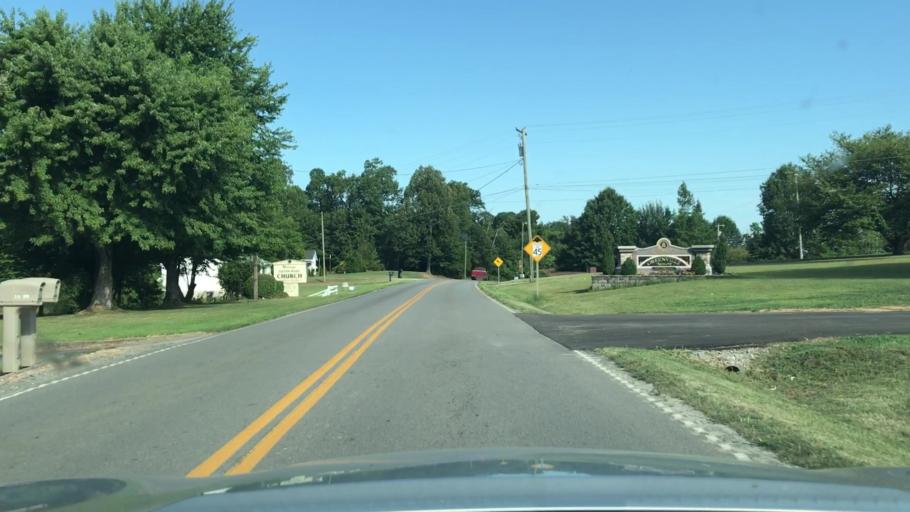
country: US
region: Kentucky
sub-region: Muhlenberg County
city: Greenville
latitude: 37.1889
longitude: -87.1694
